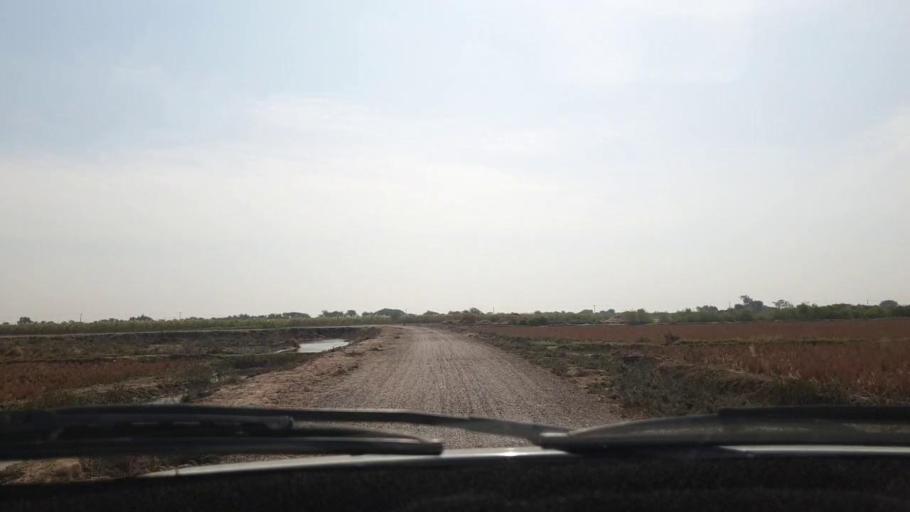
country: PK
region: Sindh
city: Bulri
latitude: 24.8627
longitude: 68.4728
